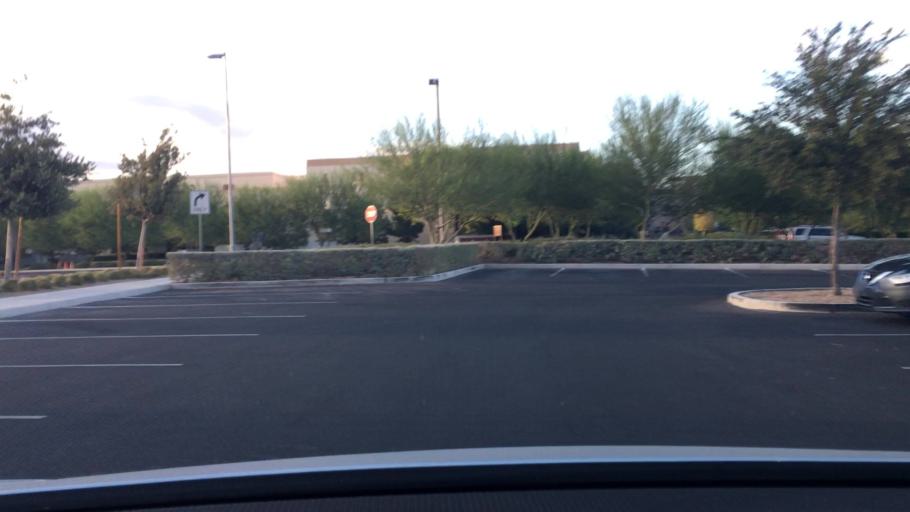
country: US
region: Nevada
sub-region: Clark County
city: Summerlin South
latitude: 36.1529
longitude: -115.3349
